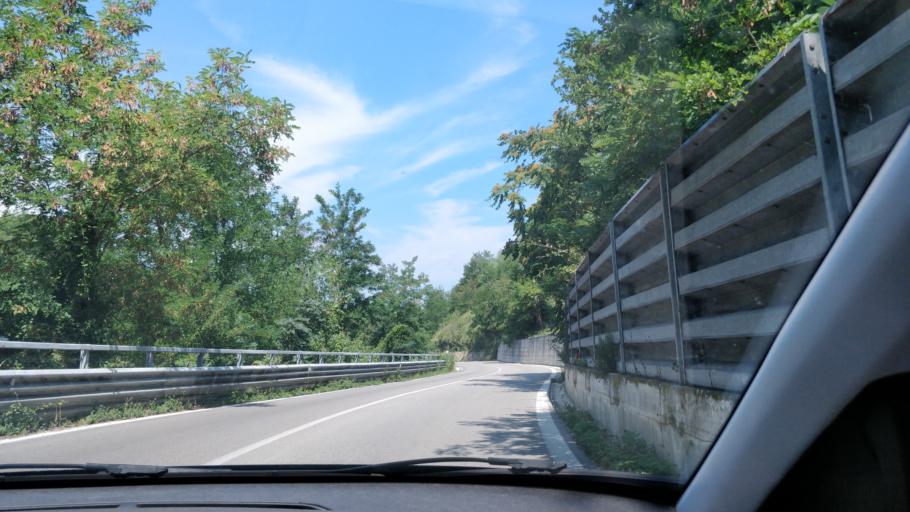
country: IT
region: Abruzzo
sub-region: Provincia di Chieti
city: Ortona
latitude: 42.3393
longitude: 14.4111
